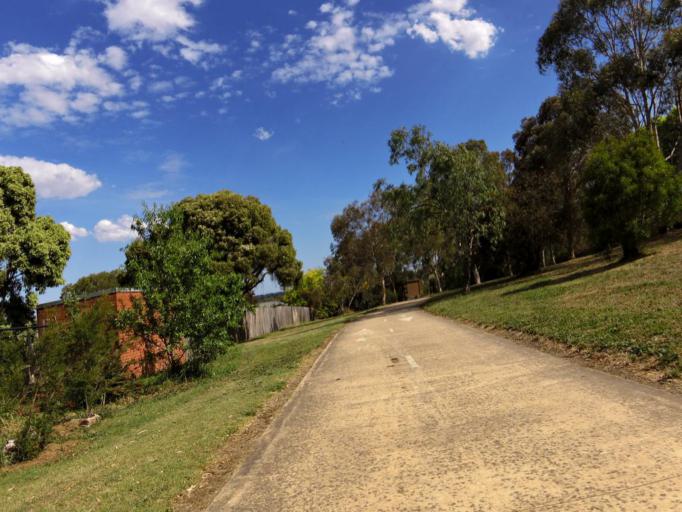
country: AU
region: Victoria
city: Rosanna
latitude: -37.7481
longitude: 145.0799
